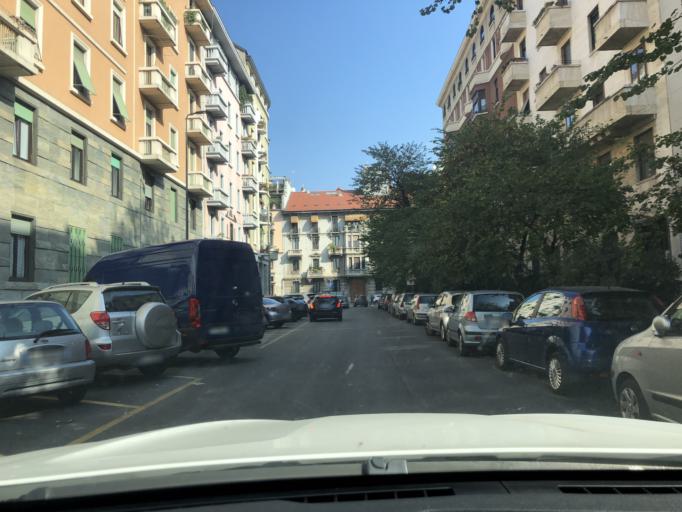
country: IT
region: Lombardy
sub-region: Citta metropolitana di Milano
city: Milano
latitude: 45.4823
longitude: 9.2108
